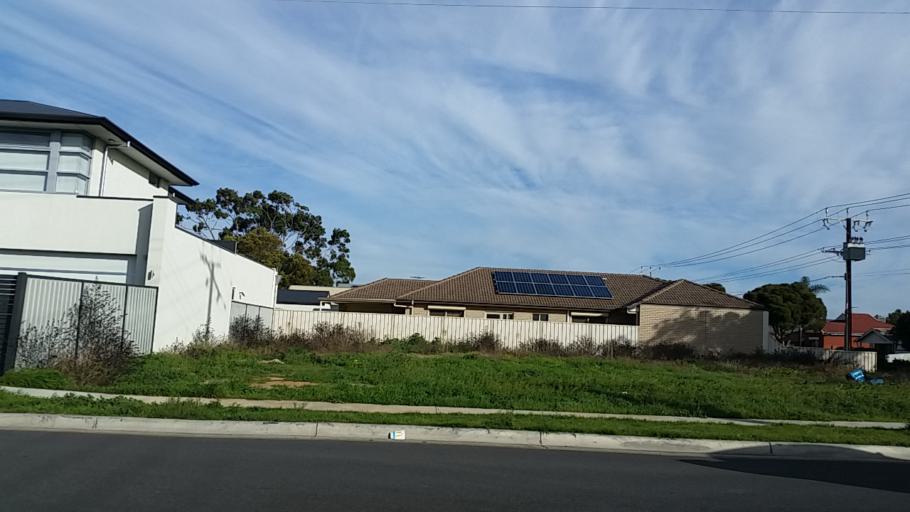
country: AU
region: South Australia
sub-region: Charles Sturt
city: Seaton
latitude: -34.8933
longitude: 138.5191
